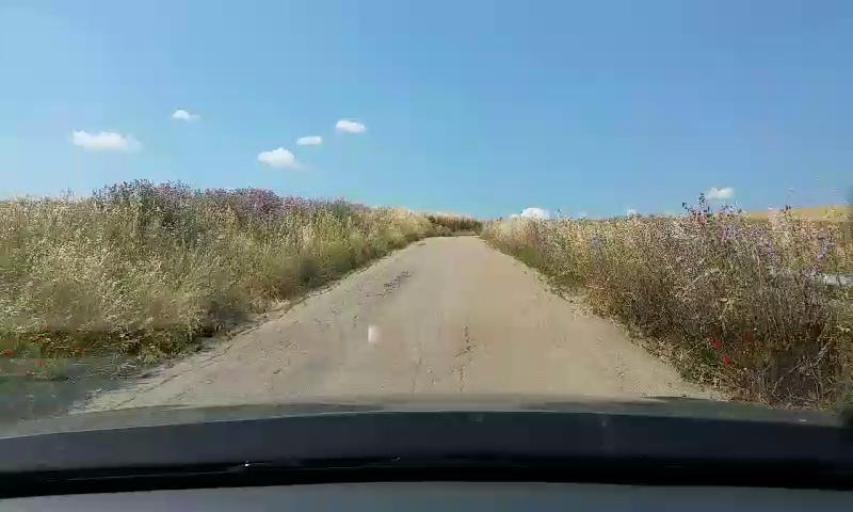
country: IT
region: Molise
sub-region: Provincia di Campobasso
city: Montecilfone
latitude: 41.9213
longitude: 14.8444
